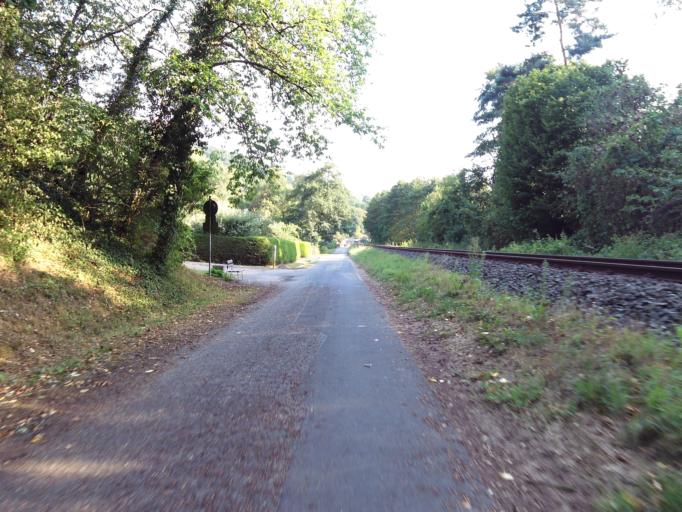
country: DE
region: Bavaria
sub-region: Regierungsbezirk Unterfranken
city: Weilbach
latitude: 49.6784
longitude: 9.2206
